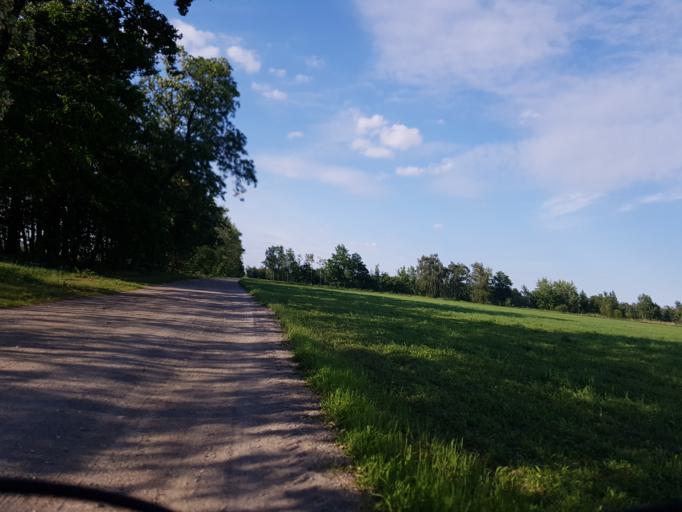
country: DE
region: Brandenburg
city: Merzdorf
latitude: 51.4288
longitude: 13.5281
